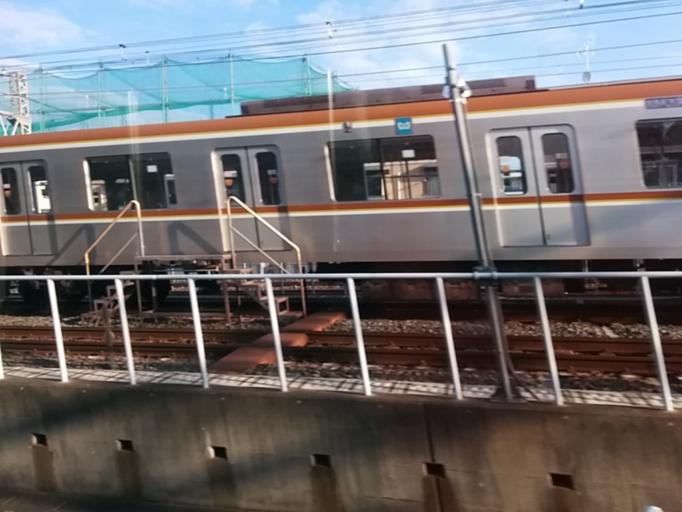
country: JP
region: Saitama
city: Wako
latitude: 35.7895
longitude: 139.6101
